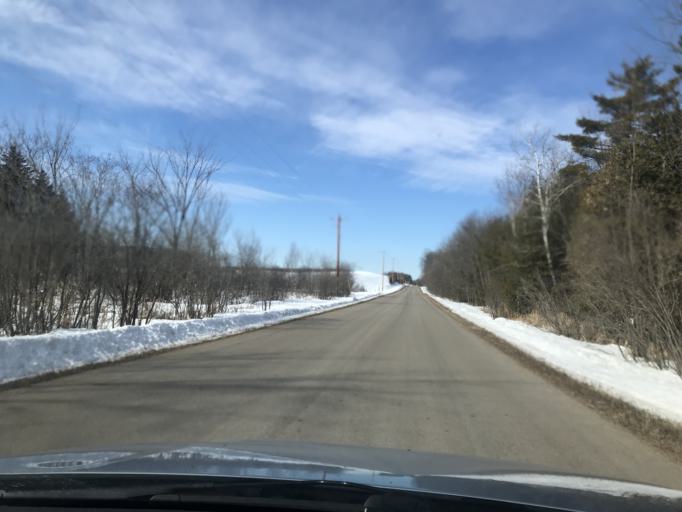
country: US
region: Wisconsin
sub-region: Oconto County
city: Gillett
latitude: 44.9617
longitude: -88.2856
